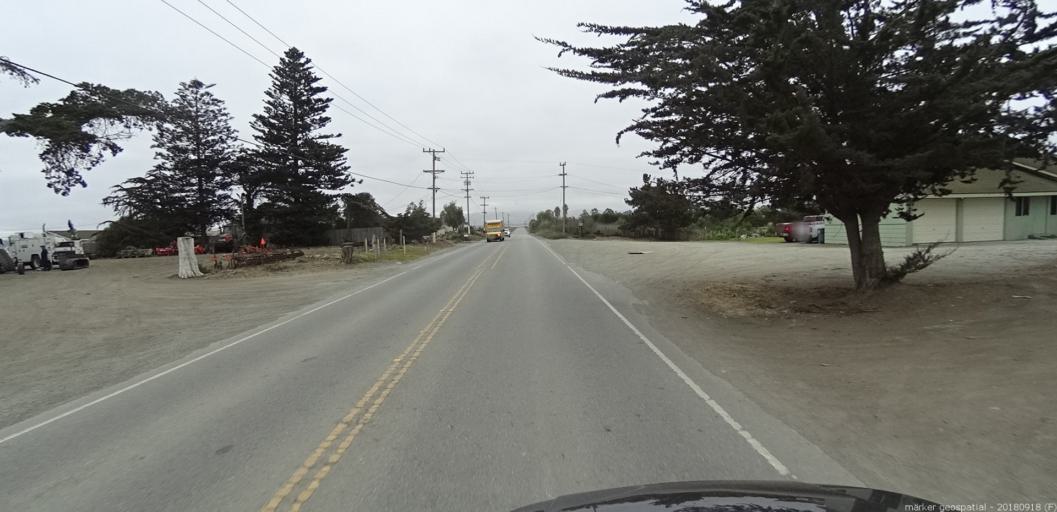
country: US
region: California
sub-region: Monterey County
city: Castroville
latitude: 36.7481
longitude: -121.7187
